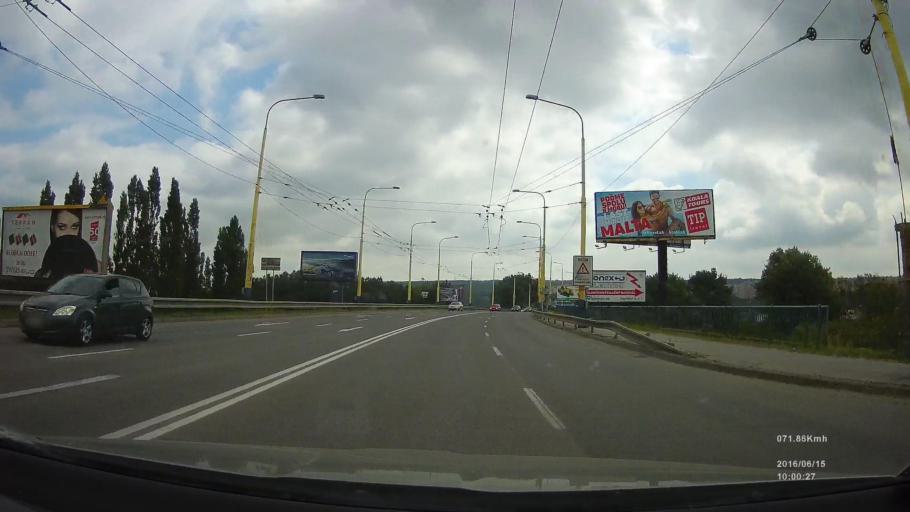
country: SK
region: Kosicky
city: Kosice
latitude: 48.7419
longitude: 21.2596
